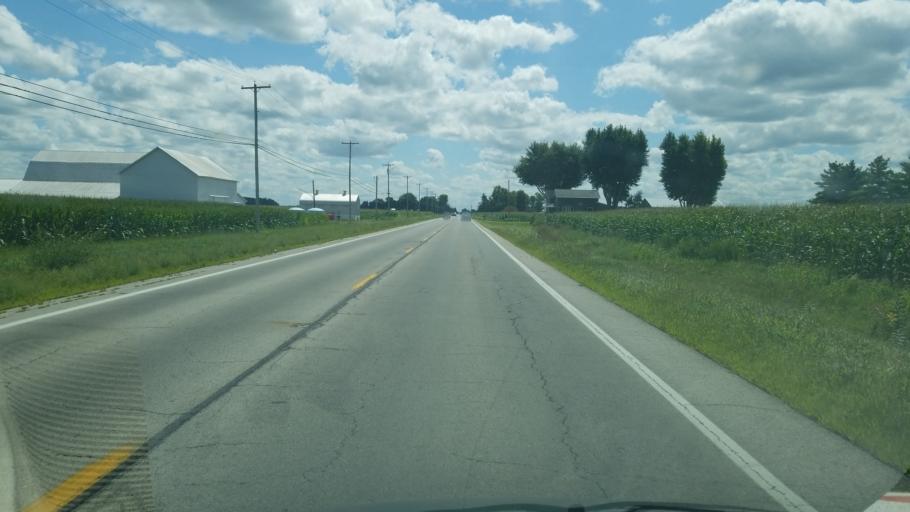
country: US
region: Ohio
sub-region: Henry County
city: Napoleon
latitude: 41.3684
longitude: -84.1203
